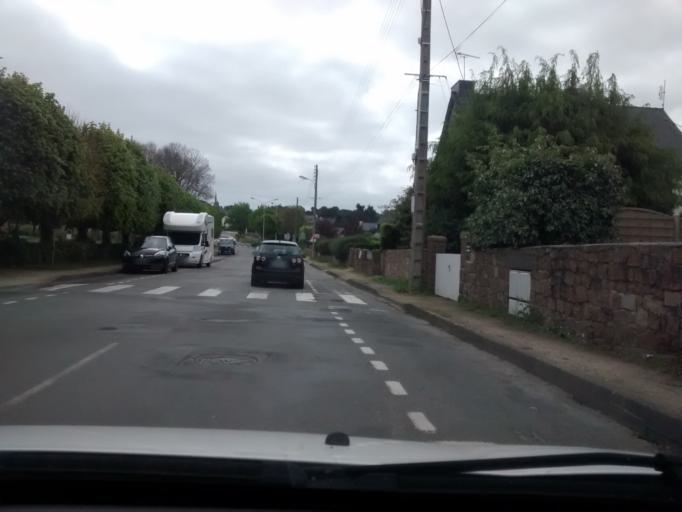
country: FR
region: Brittany
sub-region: Departement des Cotes-d'Armor
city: Tregastel
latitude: 48.8252
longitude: -3.4808
